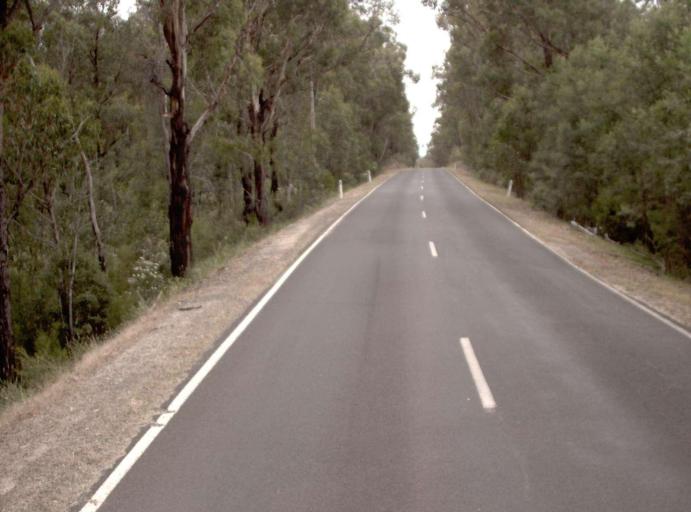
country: AU
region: Victoria
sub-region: Latrobe
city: Traralgon
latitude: -38.4726
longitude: 146.8228
